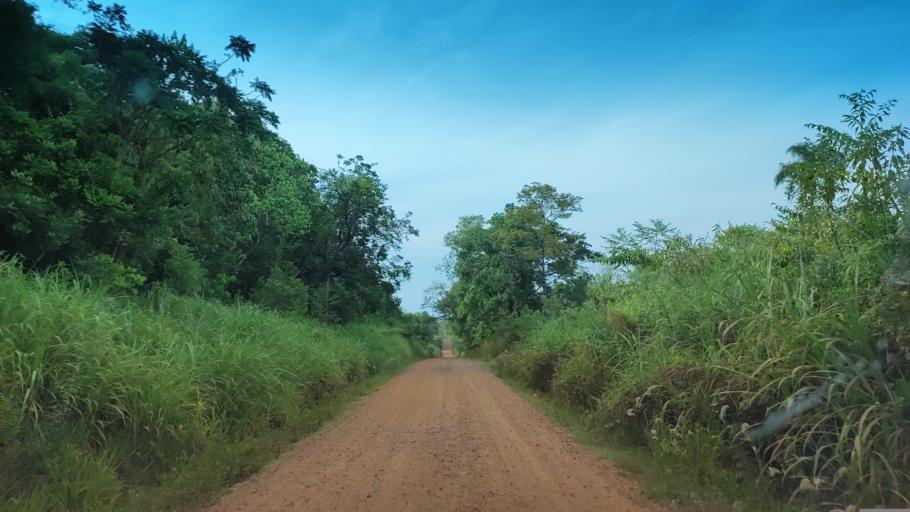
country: AR
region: Misiones
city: Gobernador Roca
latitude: -27.1540
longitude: -55.5272
